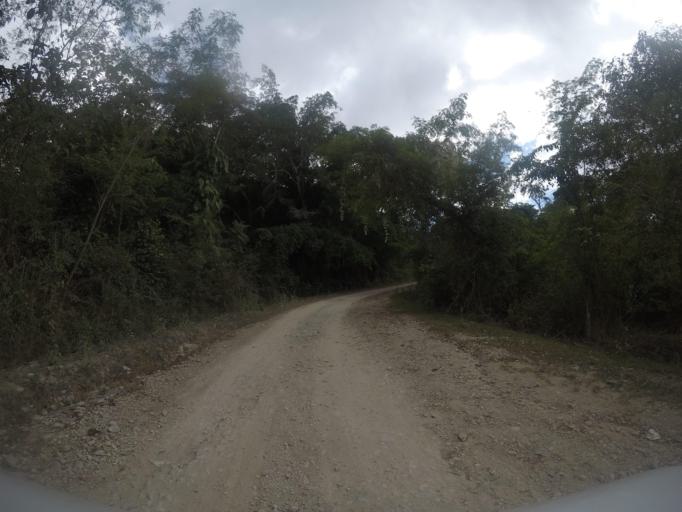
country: TL
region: Lautem
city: Lospalos
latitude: -8.5480
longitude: 126.9027
